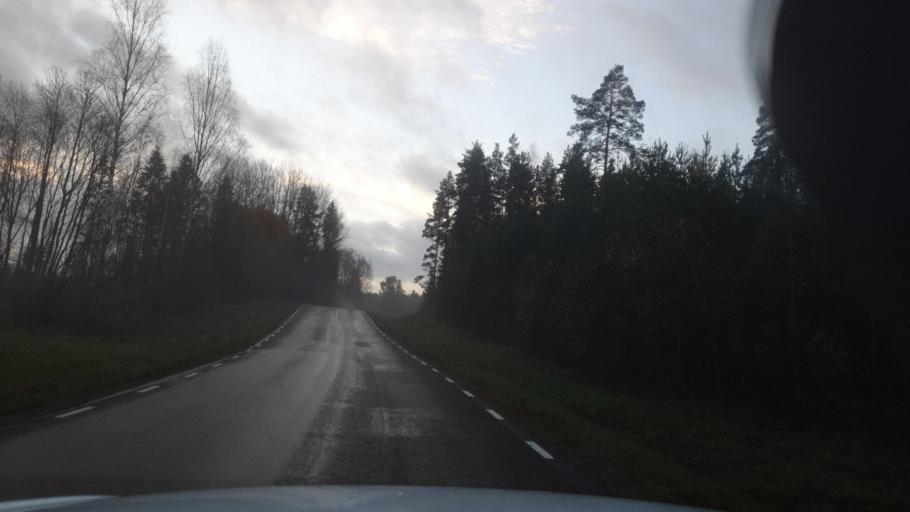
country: SE
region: Vaermland
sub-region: Arvika Kommun
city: Arvika
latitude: 59.6321
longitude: 12.7974
